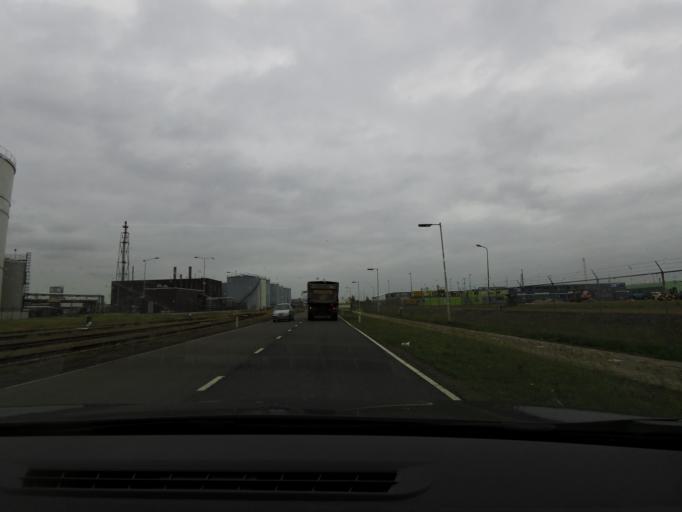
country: NL
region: South Holland
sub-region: Gemeente Vlaardingen
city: Vlaardingen
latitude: 51.8866
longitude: 4.3329
